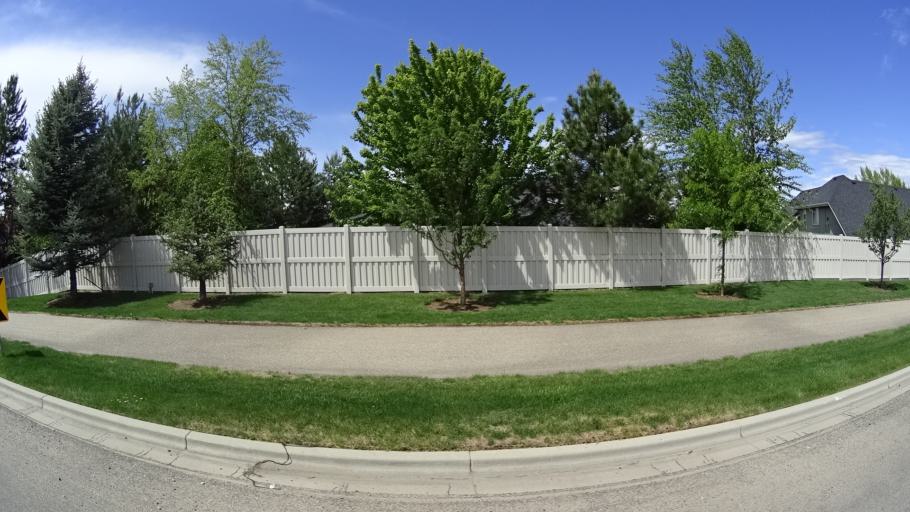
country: US
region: Idaho
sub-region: Ada County
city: Meridian
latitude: 43.5763
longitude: -116.3983
